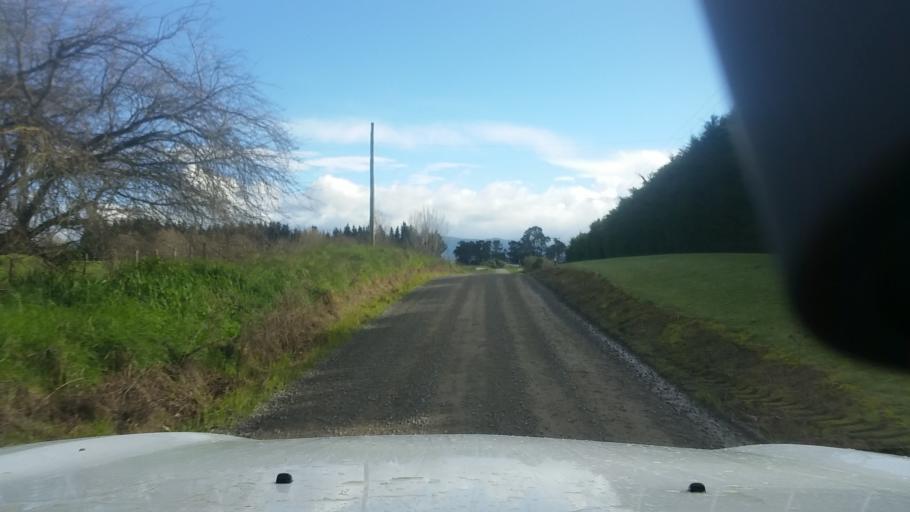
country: NZ
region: Wellington
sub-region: Masterton District
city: Masterton
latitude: -41.1368
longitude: 175.4666
